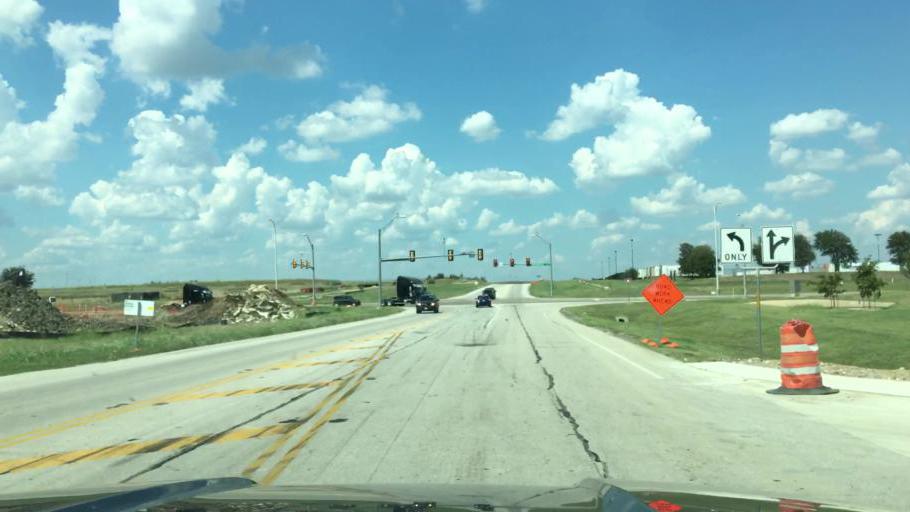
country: US
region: Texas
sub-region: Tarrant County
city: Haslet
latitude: 32.9887
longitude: -97.3422
